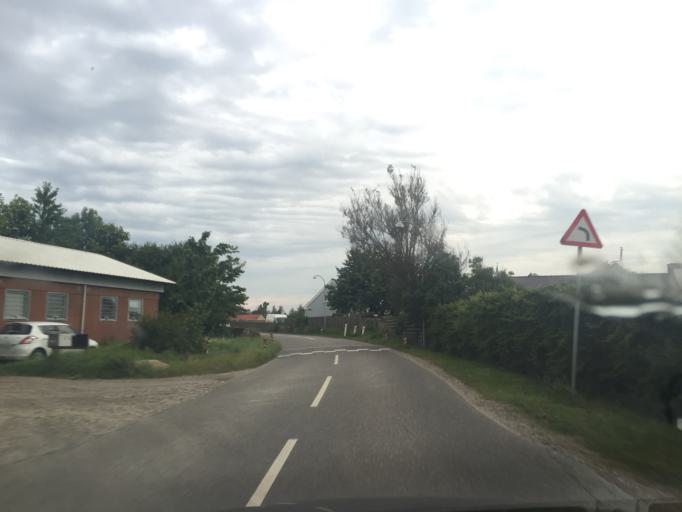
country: DK
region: Capital Region
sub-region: Egedal Kommune
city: Vekso
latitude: 55.7122
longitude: 12.2178
